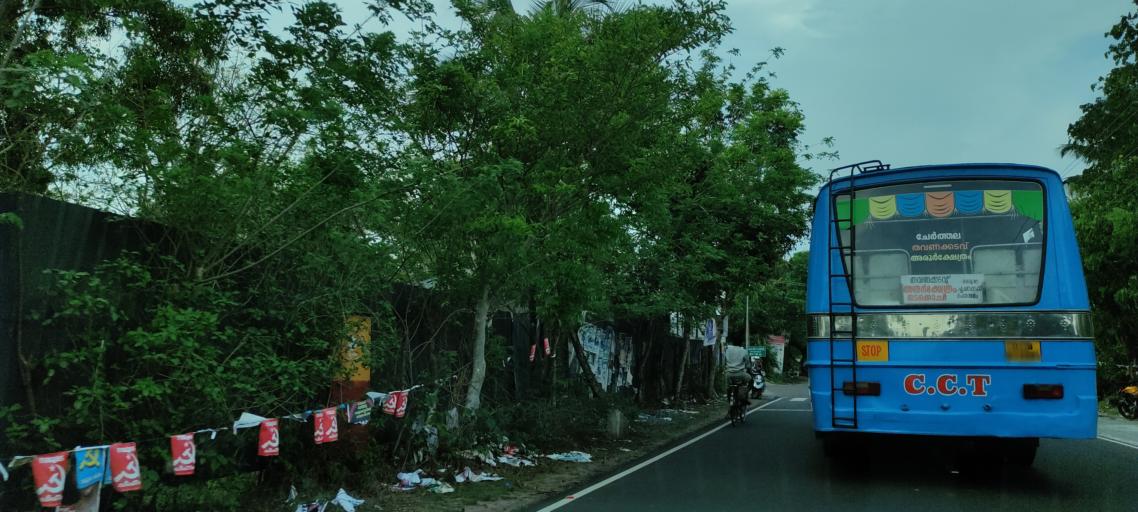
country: IN
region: Kerala
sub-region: Alappuzha
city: Kutiatodu
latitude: 9.7828
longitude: 76.3601
